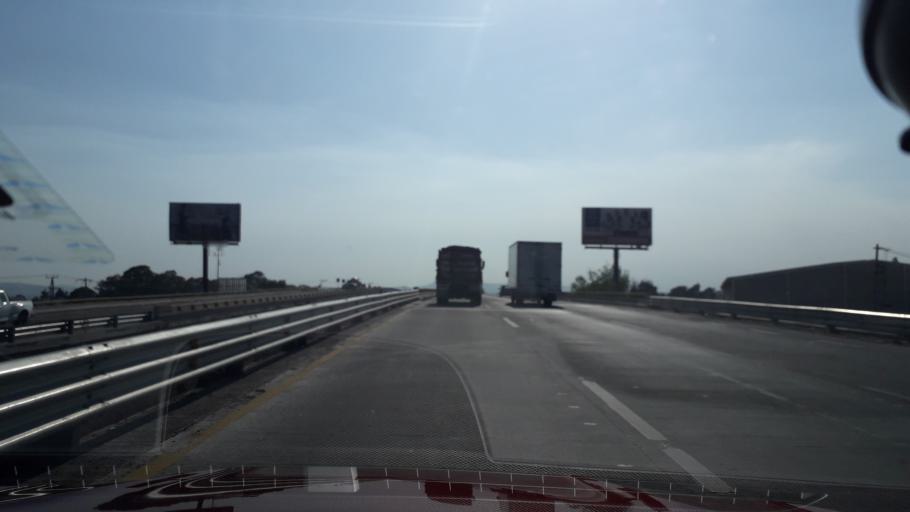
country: MX
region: Puebla
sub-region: Puebla
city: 18 de Marzo
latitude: 18.9715
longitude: -98.1972
